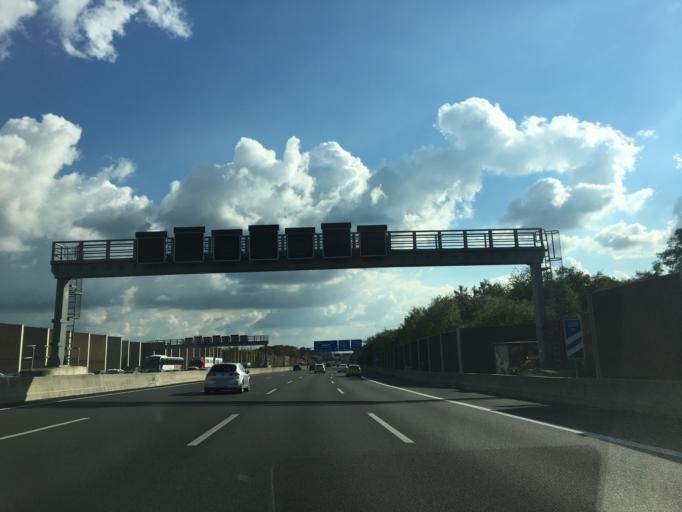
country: DE
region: North Rhine-Westphalia
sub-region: Regierungsbezirk Koln
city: Buchheim
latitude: 50.9741
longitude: 7.0282
